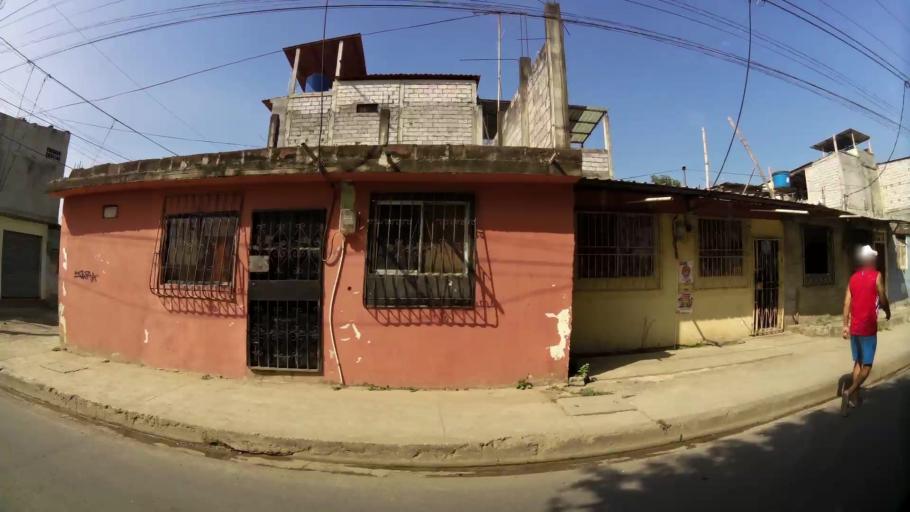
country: EC
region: Guayas
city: Eloy Alfaro
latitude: -2.1661
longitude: -79.8029
